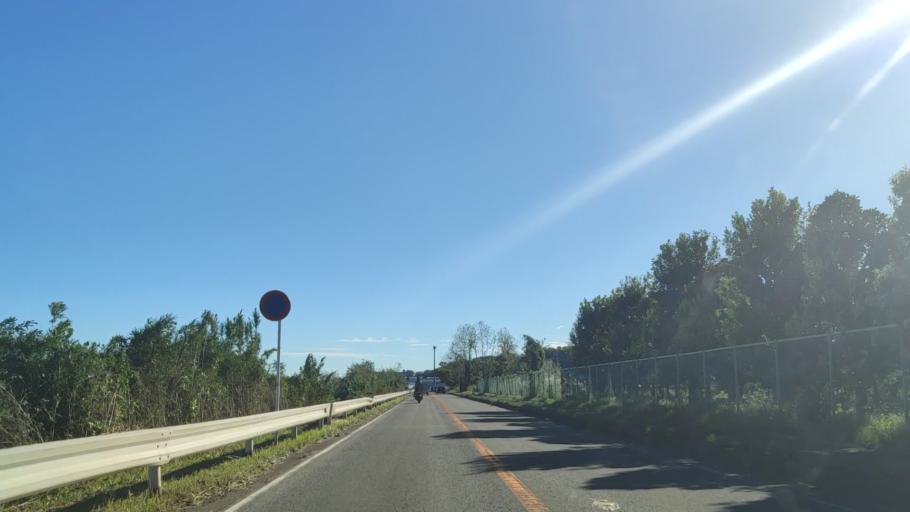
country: JP
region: Kanagawa
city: Zama
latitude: 35.5004
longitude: 139.3715
